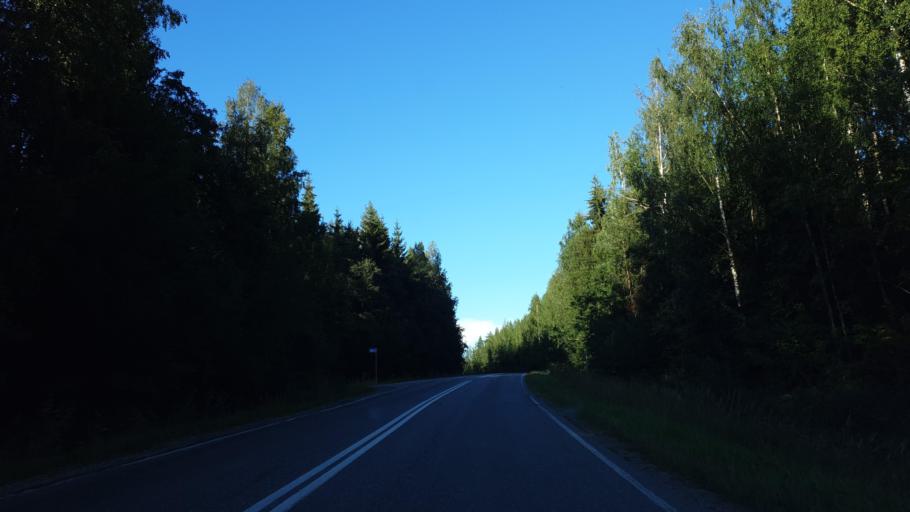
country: FI
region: Northern Savo
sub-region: Koillis-Savo
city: Juankoski
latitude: 63.0985
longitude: 28.4307
